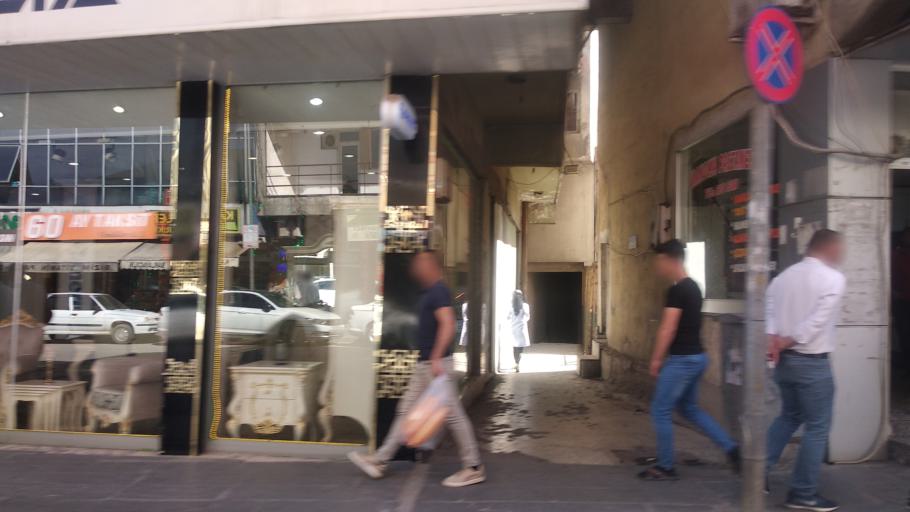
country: TR
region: Bitlis
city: Bitlis
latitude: 38.4018
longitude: 42.1092
